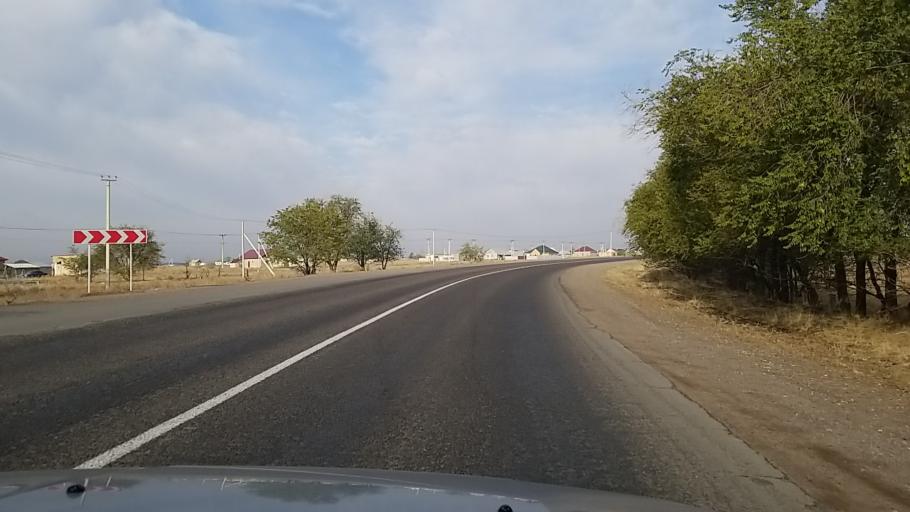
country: KZ
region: Almaty Oblysy
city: Burunday
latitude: 43.4778
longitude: 76.6812
